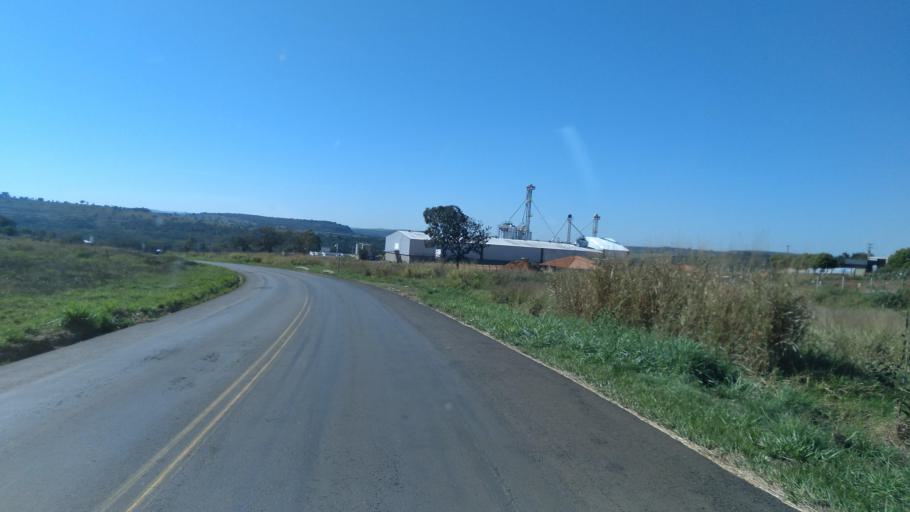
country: BR
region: Goias
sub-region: Mineiros
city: Mineiros
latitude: -17.5797
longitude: -52.5151
